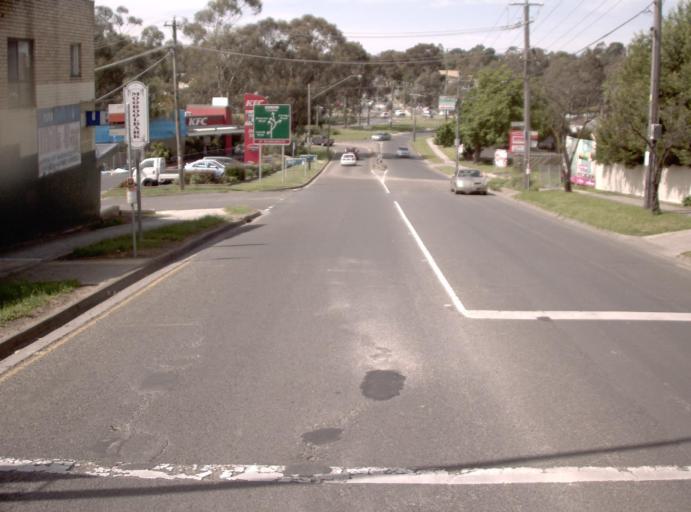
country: AU
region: Victoria
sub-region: Maroondah
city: Croydon North
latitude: -37.7905
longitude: 145.3077
